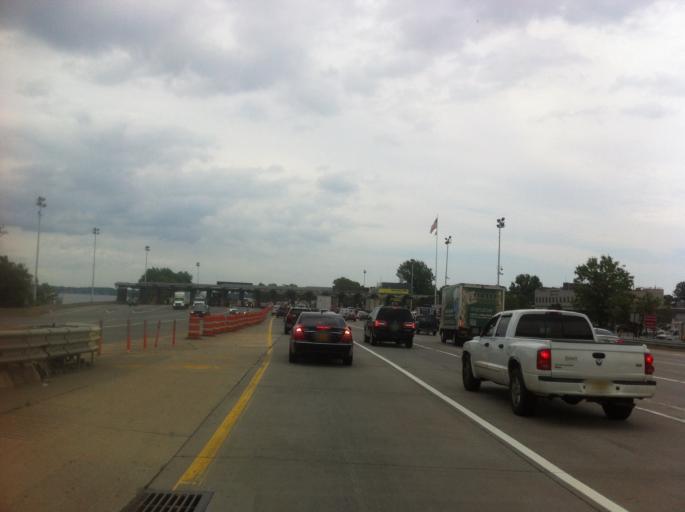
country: US
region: New York
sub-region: Nassau County
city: East Atlantic Beach
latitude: 40.8182
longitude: -73.8059
